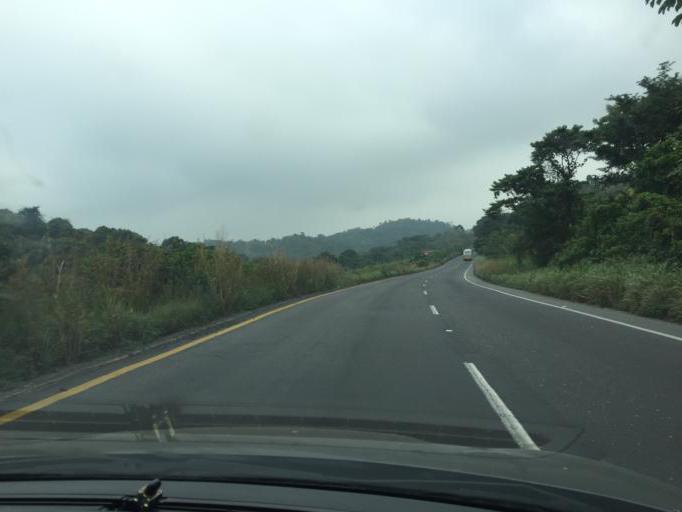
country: MX
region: Veracruz
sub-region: Moloacan
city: Tlacuilolapan
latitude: 18.0527
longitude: -94.2161
